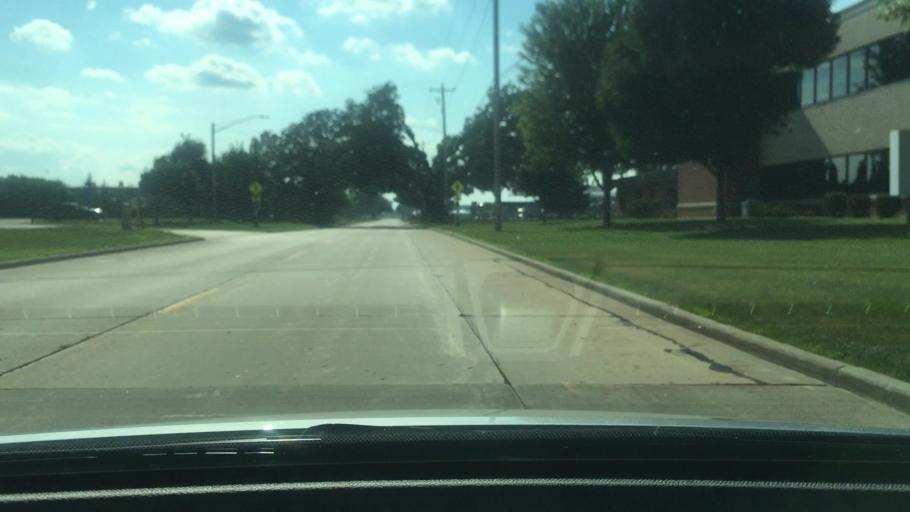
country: US
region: Wisconsin
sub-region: Winnebago County
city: Oshkosh
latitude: 43.9812
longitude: -88.5458
